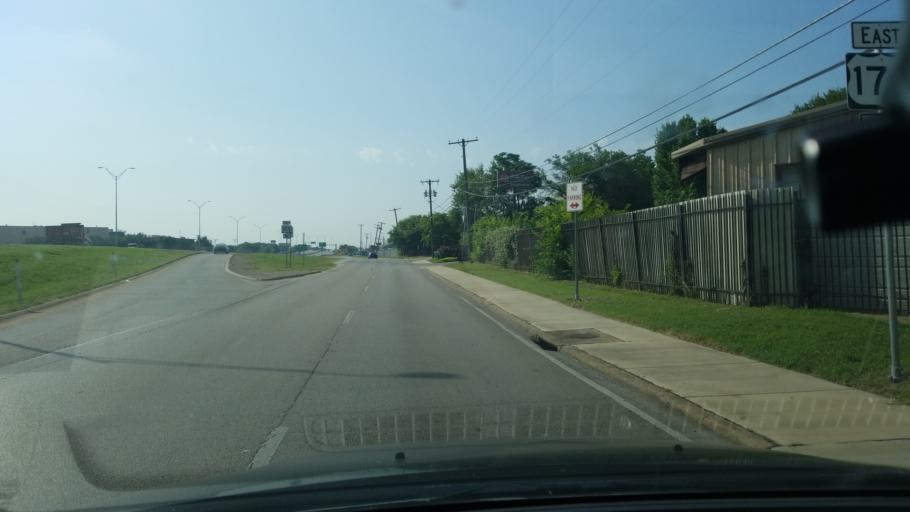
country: US
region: Texas
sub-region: Dallas County
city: Balch Springs
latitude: 32.7173
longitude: -96.6905
